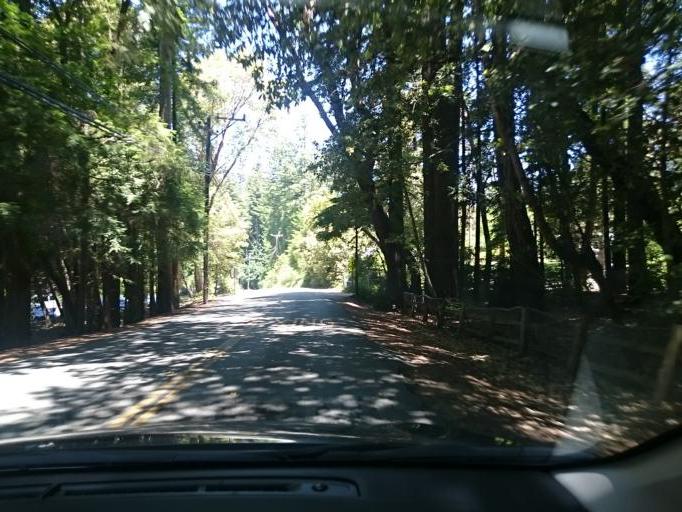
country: US
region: California
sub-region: Santa Cruz County
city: Bonny Doon
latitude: 37.0614
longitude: -122.1475
